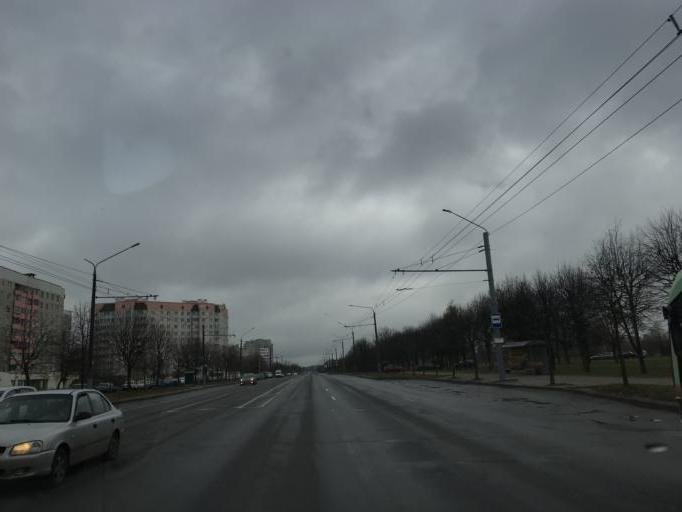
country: BY
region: Mogilev
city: Mahilyow
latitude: 53.8689
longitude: 30.3264
